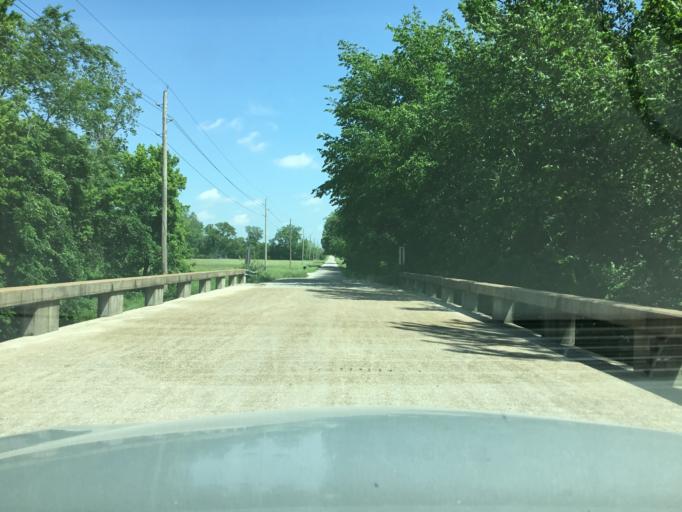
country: US
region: Kansas
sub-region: Labette County
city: Parsons
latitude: 37.3487
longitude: -95.2496
